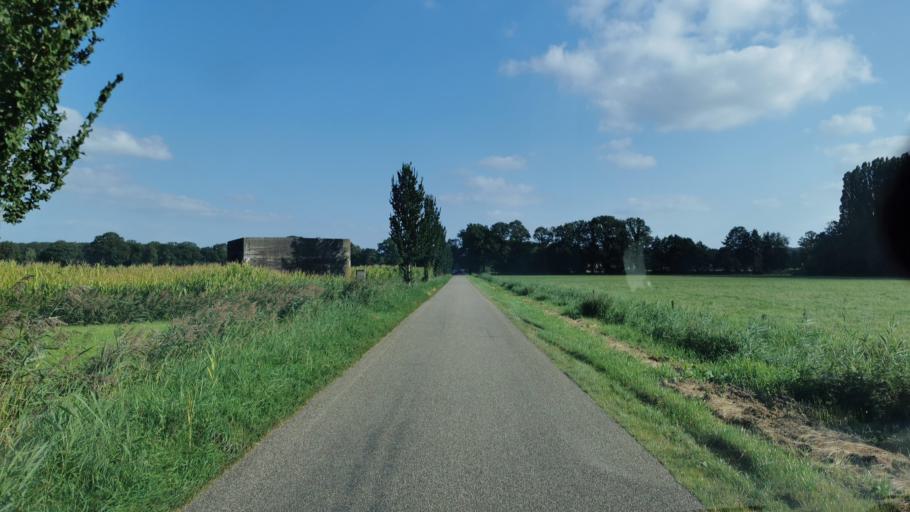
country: NL
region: Overijssel
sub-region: Gemeente Borne
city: Borne
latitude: 52.3284
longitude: 6.7731
